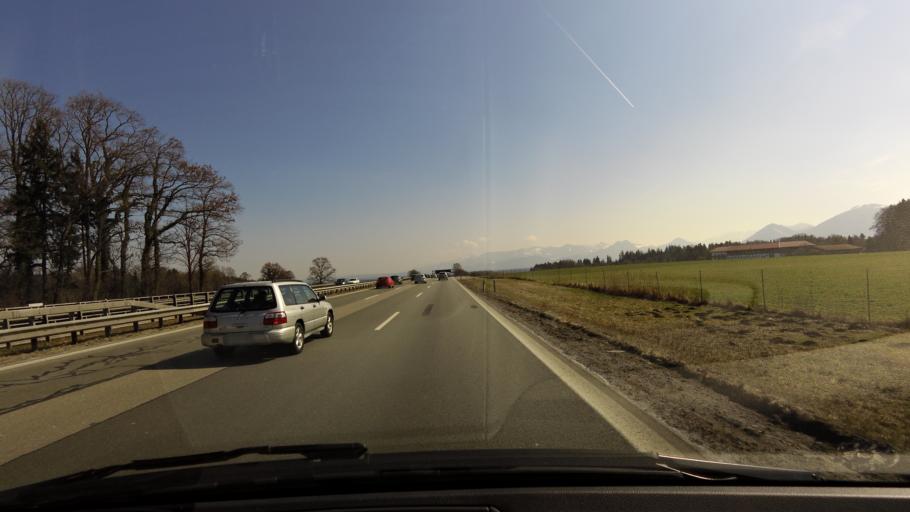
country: DE
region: Bavaria
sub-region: Upper Bavaria
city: Irschenberg
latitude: 47.8269
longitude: 11.9509
